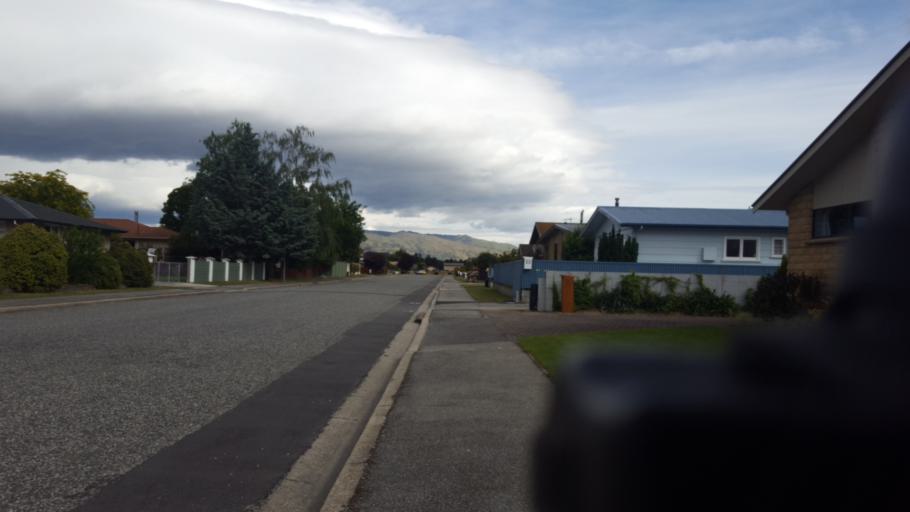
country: NZ
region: Otago
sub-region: Queenstown-Lakes District
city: Wanaka
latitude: -45.2424
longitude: 169.3933
